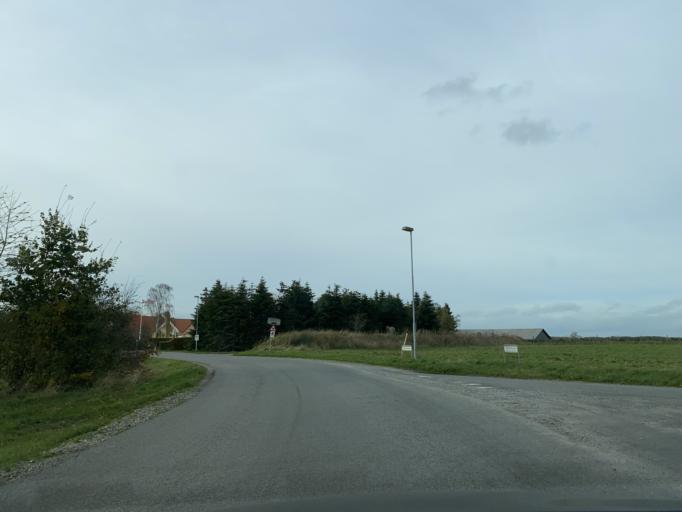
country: DK
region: Central Jutland
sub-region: Arhus Kommune
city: Framlev
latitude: 56.1646
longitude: 9.9960
